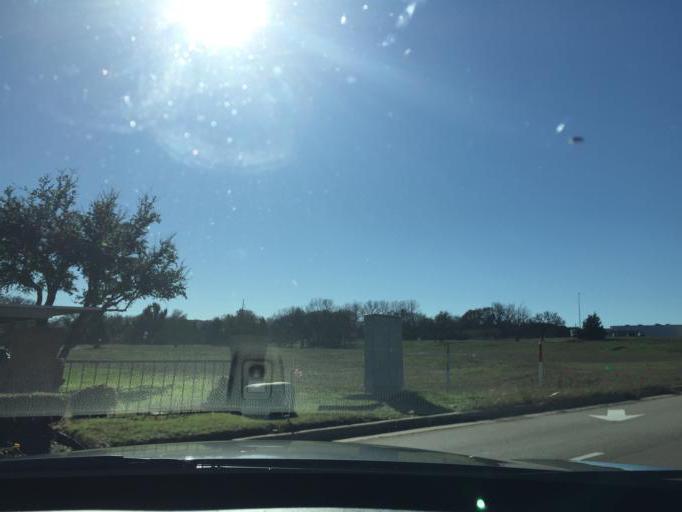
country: US
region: Texas
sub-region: Parker County
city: Weatherford
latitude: 32.7388
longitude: -97.7907
